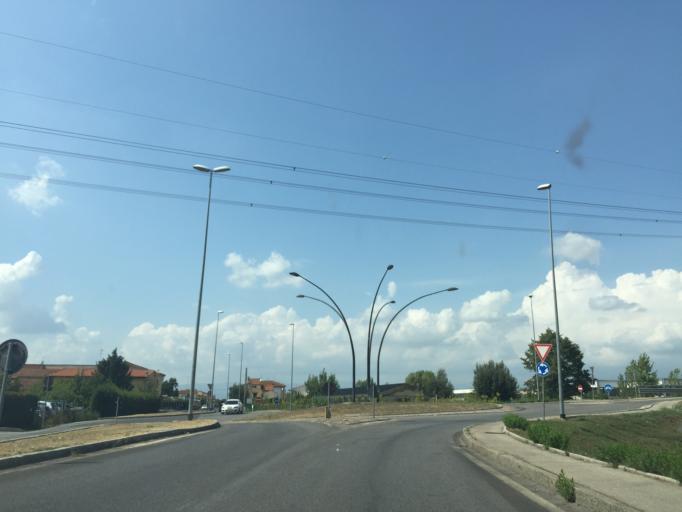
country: IT
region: Tuscany
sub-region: Provincia di Prato
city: Poggetto
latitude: 43.8324
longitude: 11.0326
